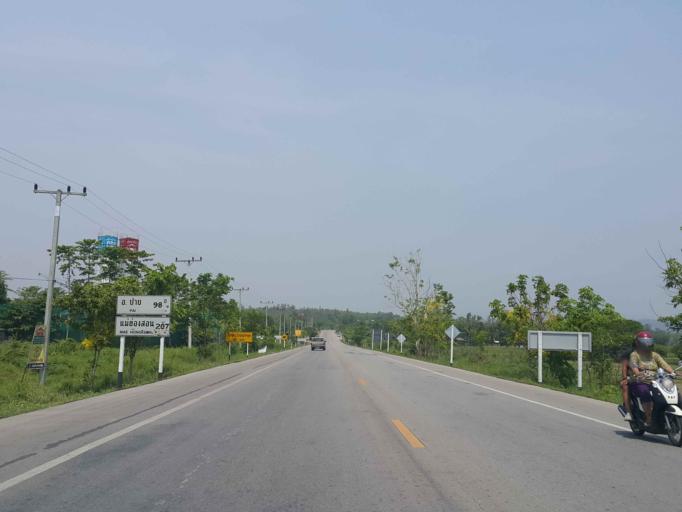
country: TH
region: Chiang Mai
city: Mae Taeng
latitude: 19.0727
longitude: 98.9367
